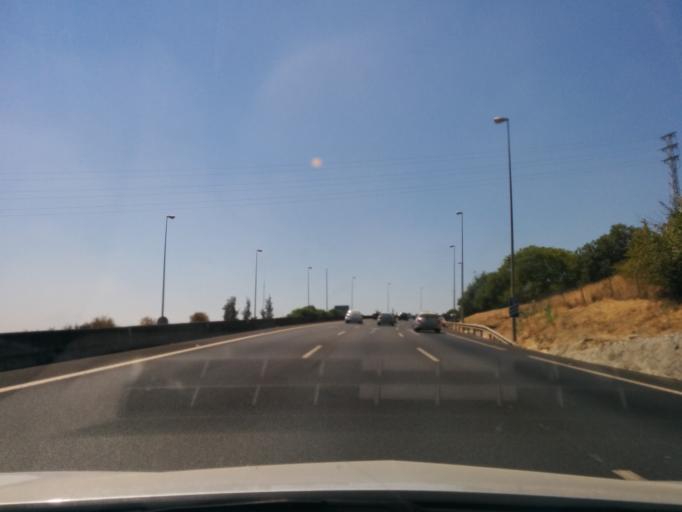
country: ES
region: Andalusia
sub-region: Provincia de Sevilla
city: Tomares
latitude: 37.3844
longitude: -6.0345
